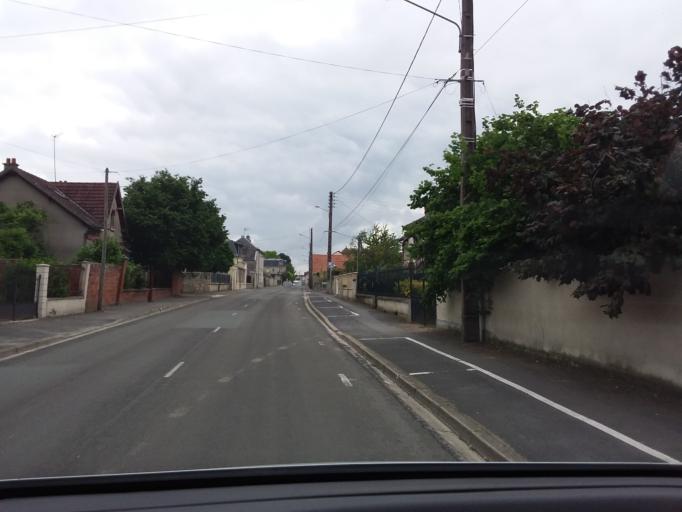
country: FR
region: Picardie
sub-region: Departement de l'Aisne
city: Vailly-sur-Aisne
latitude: 49.4079
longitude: 3.5130
